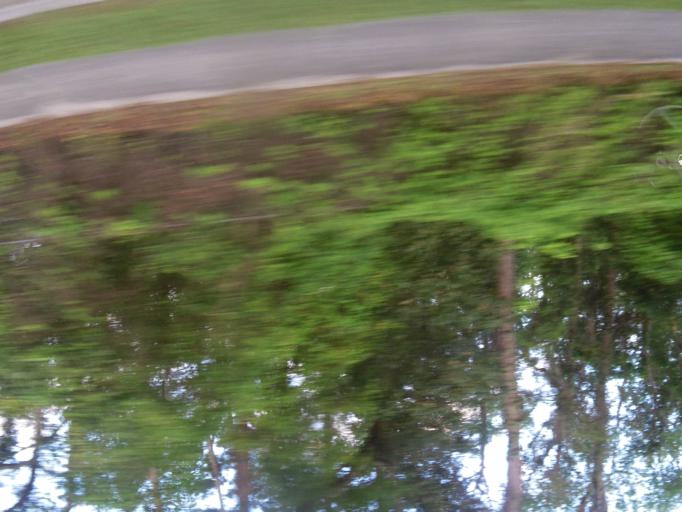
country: US
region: Florida
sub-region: Duval County
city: Jacksonville
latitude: 30.4637
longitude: -81.6178
